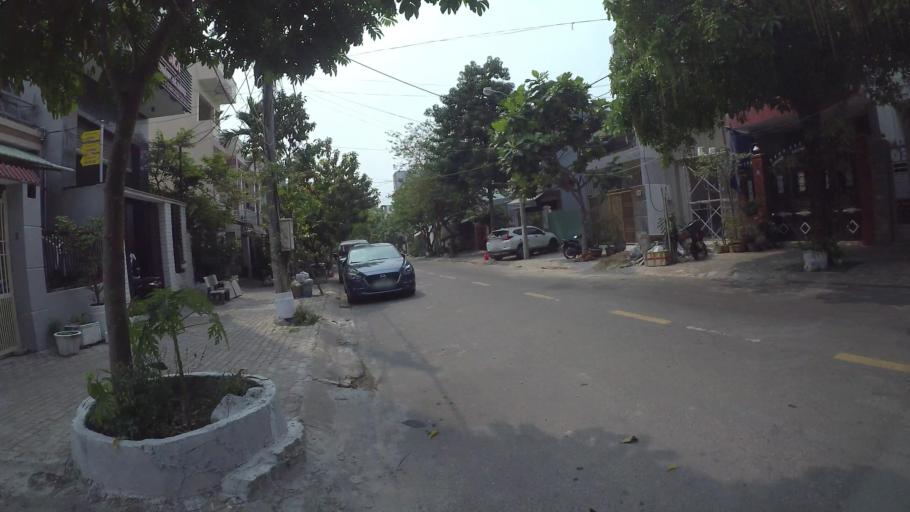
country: VN
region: Da Nang
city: Son Tra
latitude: 16.0396
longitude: 108.2197
